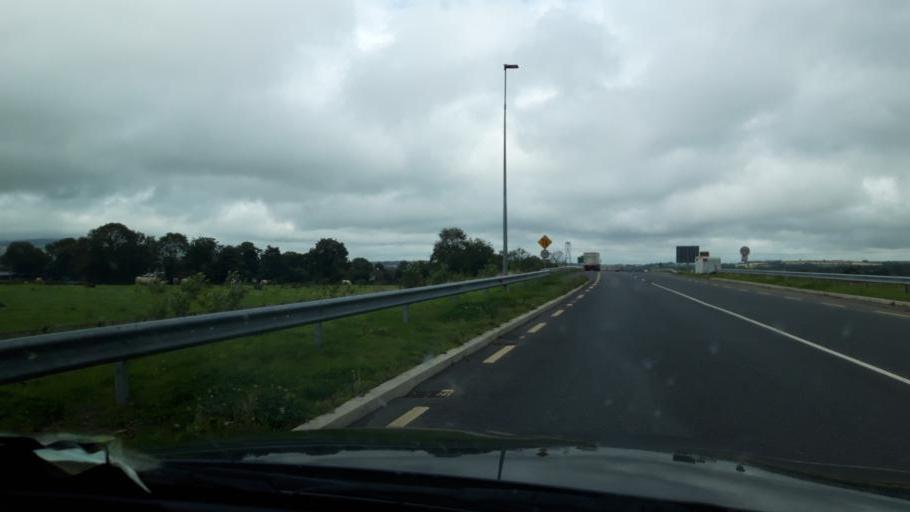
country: IE
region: Leinster
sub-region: Loch Garman
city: New Ross
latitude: 52.4190
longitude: -6.8599
